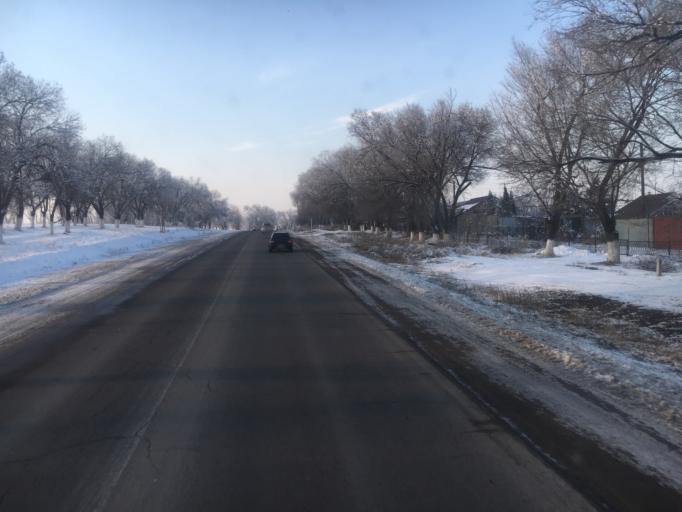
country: KZ
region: Almaty Oblysy
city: Burunday
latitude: 43.3064
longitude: 76.6688
